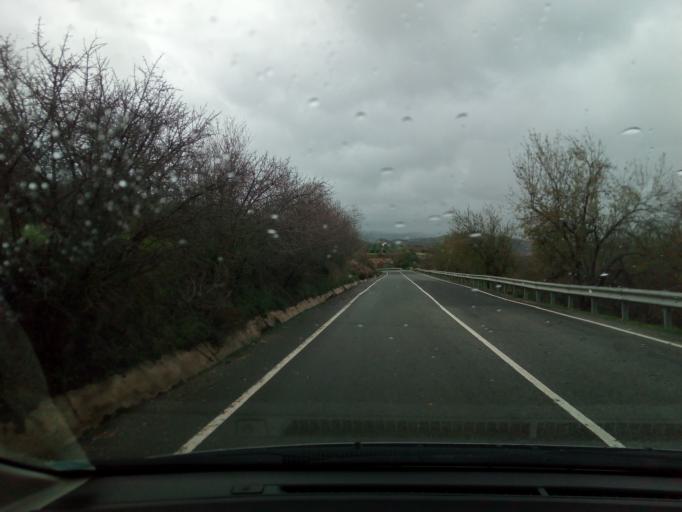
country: CY
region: Pafos
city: Polis
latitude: 34.9505
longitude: 32.4896
